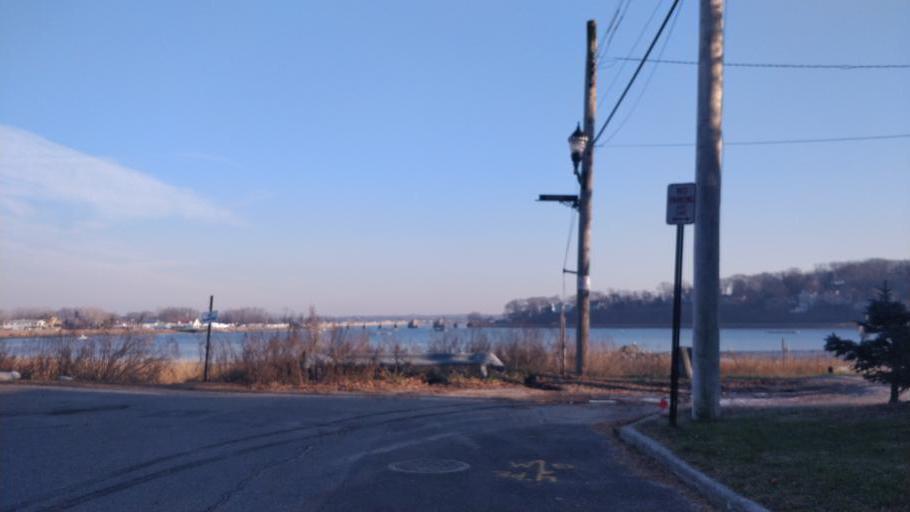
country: US
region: New York
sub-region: Nassau County
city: Bayville
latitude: 40.9050
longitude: -73.5584
